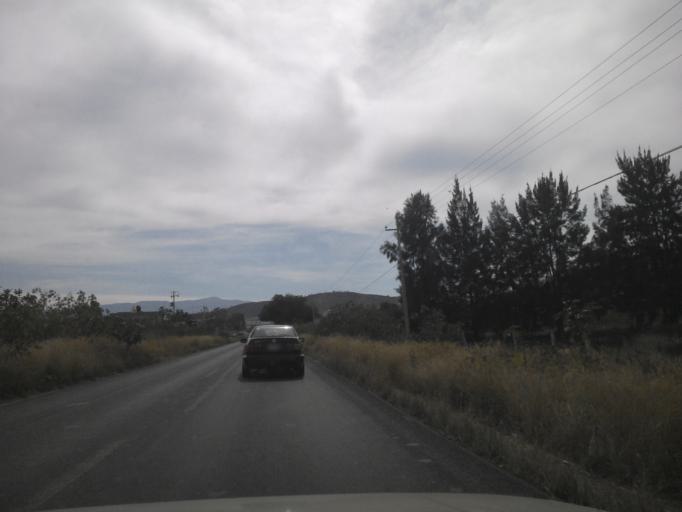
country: MX
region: Jalisco
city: San Sebastian el Grande
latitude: 20.5052
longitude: -103.4143
